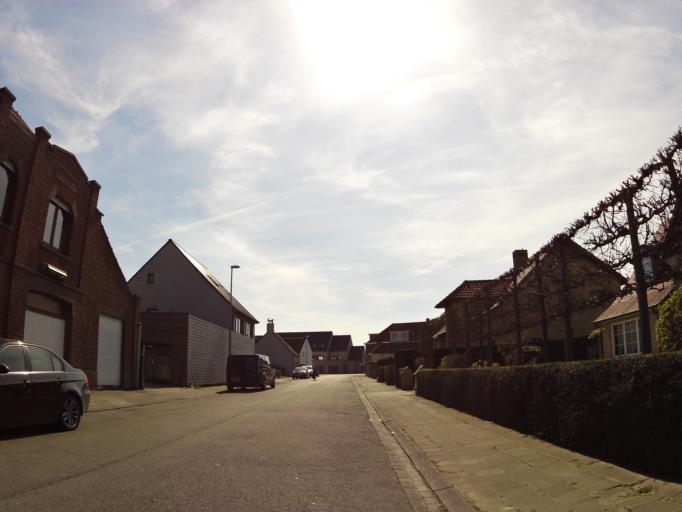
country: BE
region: Flanders
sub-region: Provincie West-Vlaanderen
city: Oudenburg
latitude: 51.1850
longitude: 3.0137
